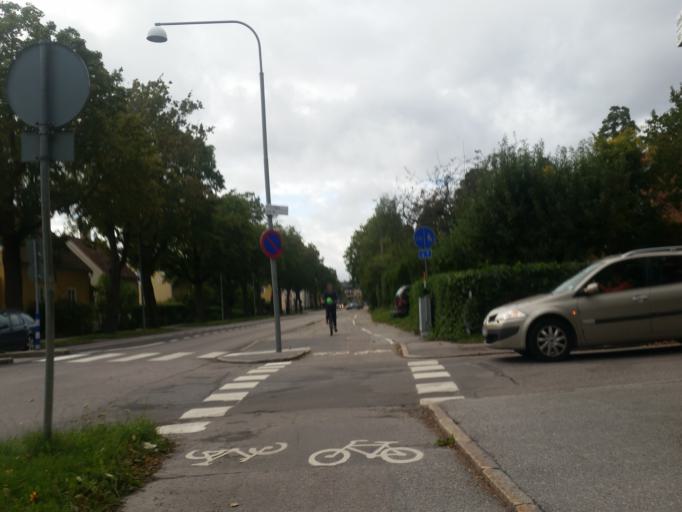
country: SE
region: Stockholm
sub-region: Stockholms Kommun
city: Arsta
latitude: 59.2821
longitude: 18.1044
